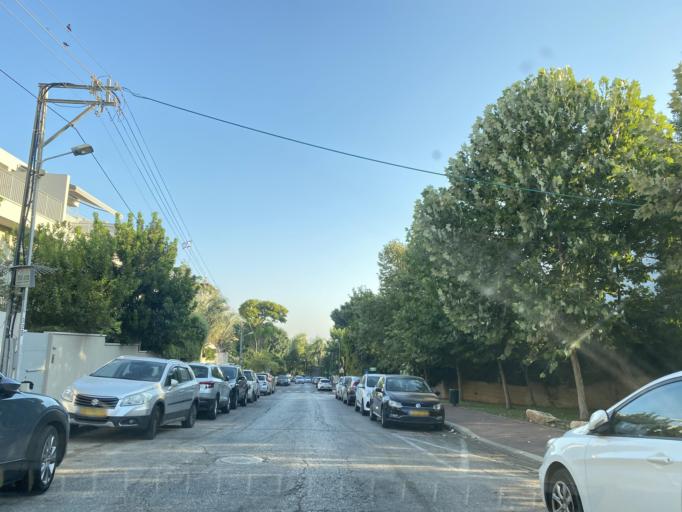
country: IL
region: Tel Aviv
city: Ramat HaSharon
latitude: 32.1421
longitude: 34.8447
